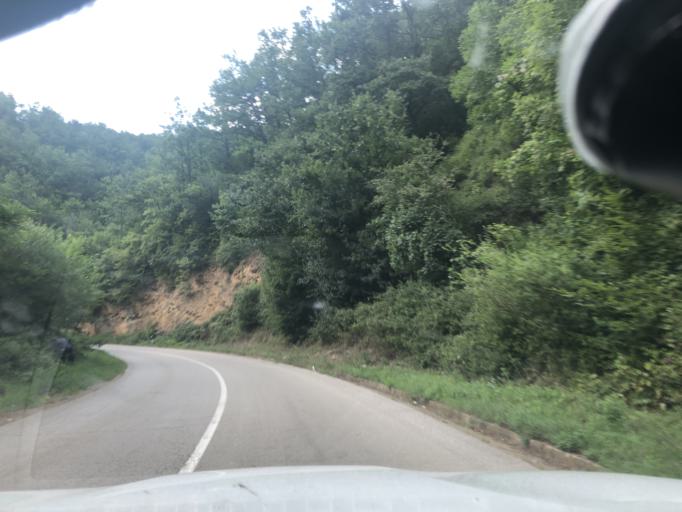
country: RS
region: Central Serbia
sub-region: Jablanicki Okrug
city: Medvega
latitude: 42.7812
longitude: 21.5972
